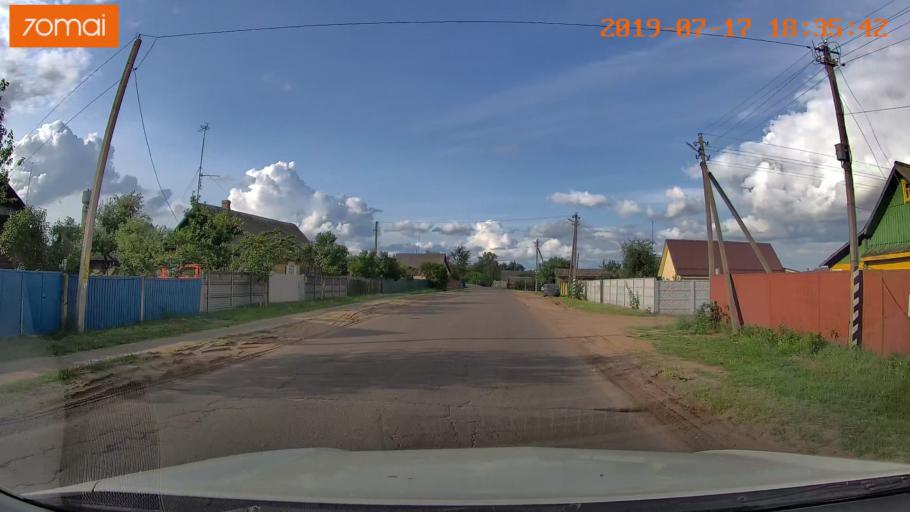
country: BY
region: Mogilev
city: Asipovichy
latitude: 53.2944
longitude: 28.6591
